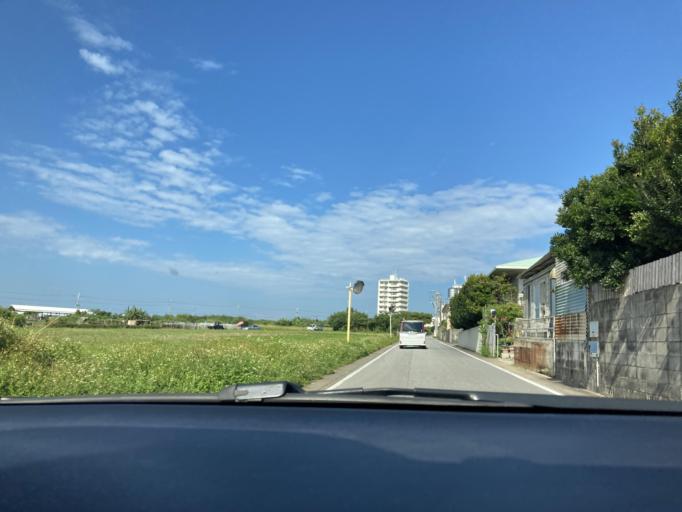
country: JP
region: Okinawa
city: Chatan
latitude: 26.3659
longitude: 127.7397
